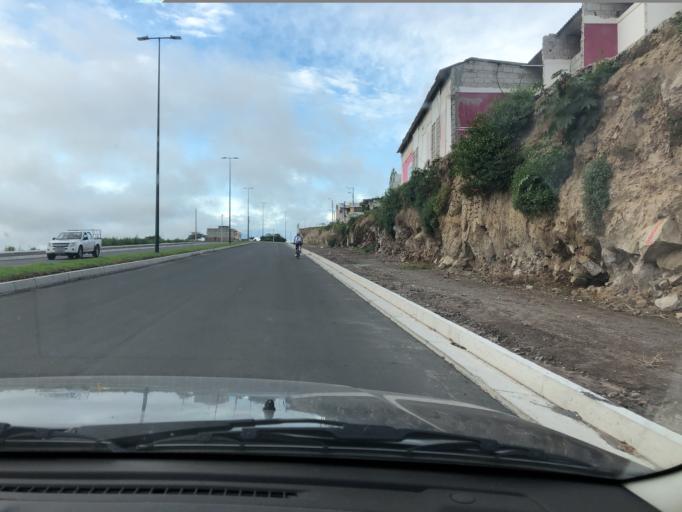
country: EC
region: Imbabura
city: Ibarra
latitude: 0.3499
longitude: -78.1410
